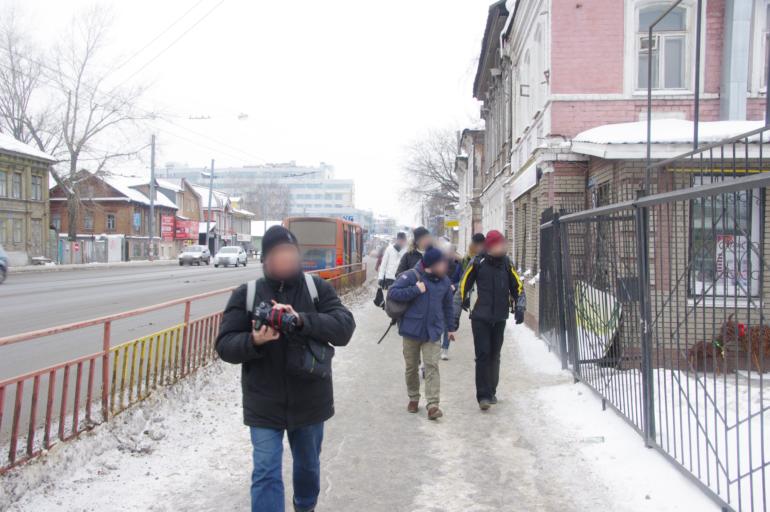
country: RU
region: Nizjnij Novgorod
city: Nizhniy Novgorod
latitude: 56.3221
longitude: 44.0374
